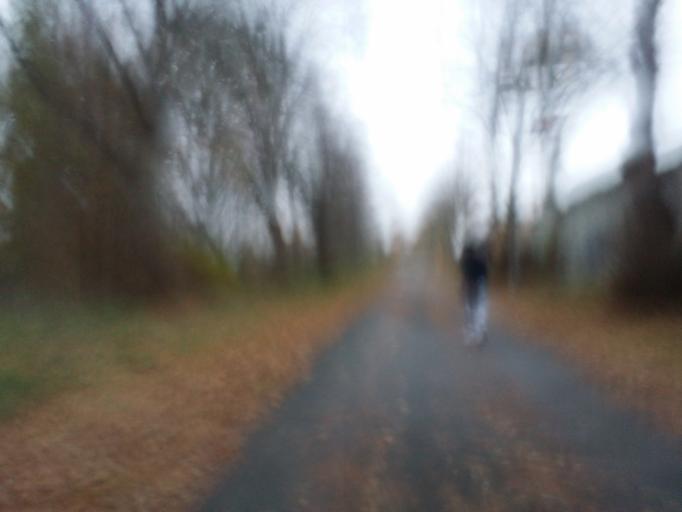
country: DE
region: Lower Saxony
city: Stuhr
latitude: 53.0241
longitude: 8.7999
